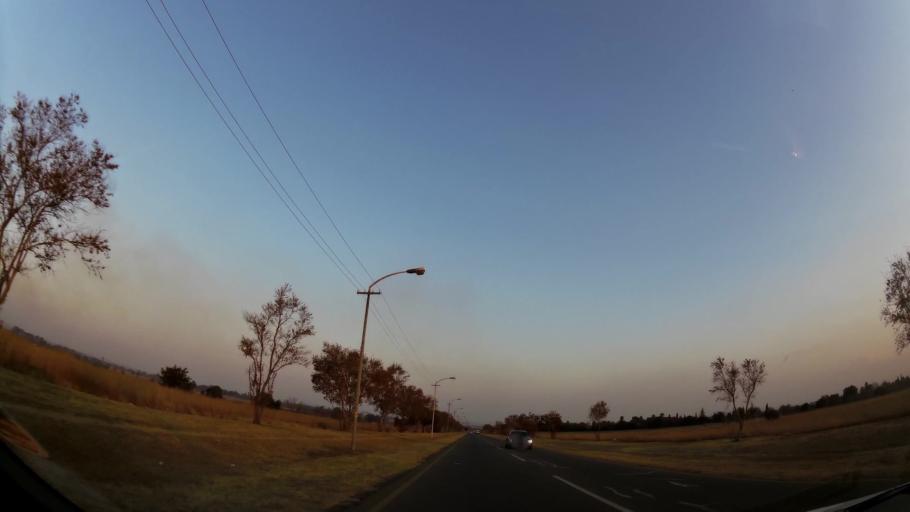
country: ZA
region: Gauteng
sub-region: Ekurhuleni Metropolitan Municipality
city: Springs
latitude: -26.3193
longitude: 28.4488
